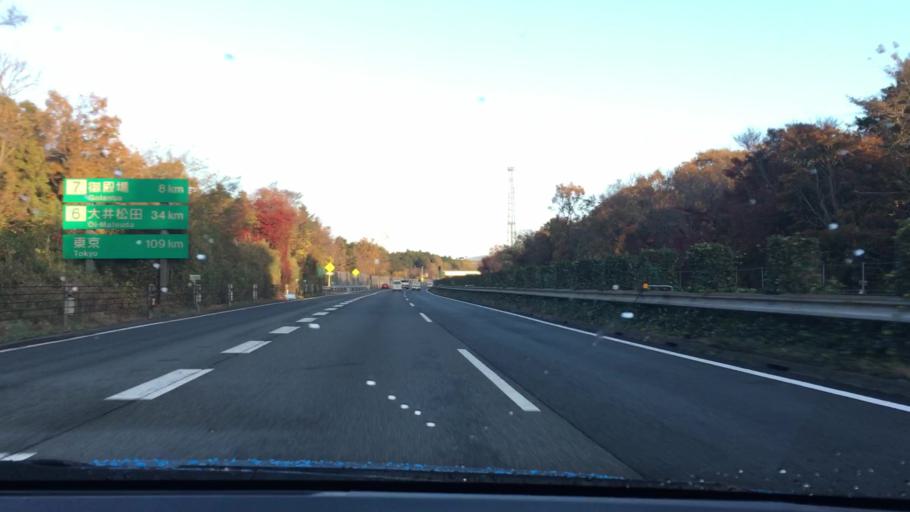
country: JP
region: Shizuoka
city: Gotemba
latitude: 35.2332
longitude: 138.9095
